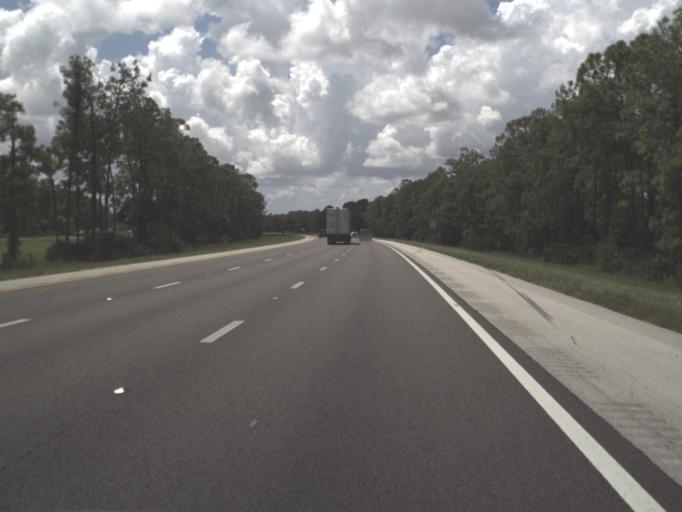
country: US
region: Florida
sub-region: Collier County
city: Vineyards
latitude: 26.2627
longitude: -81.7428
